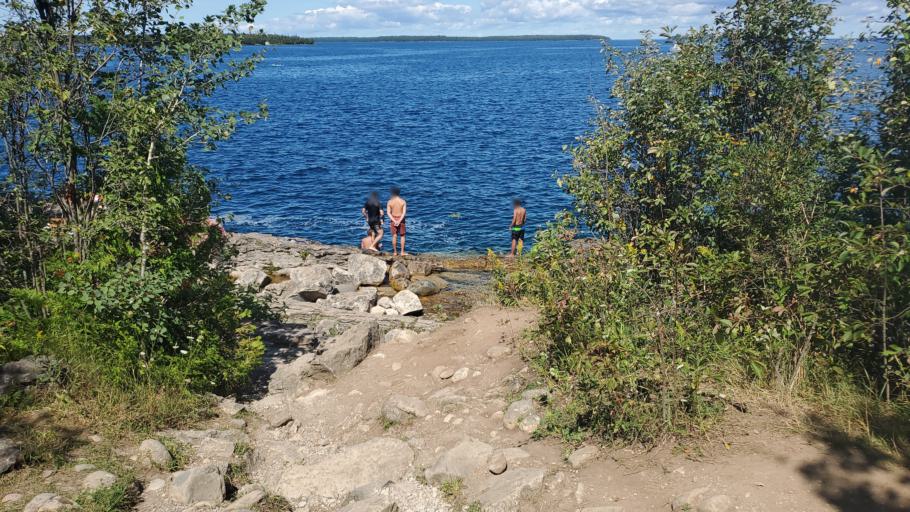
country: CA
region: Ontario
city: Tobermory
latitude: 45.2570
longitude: -81.6689
